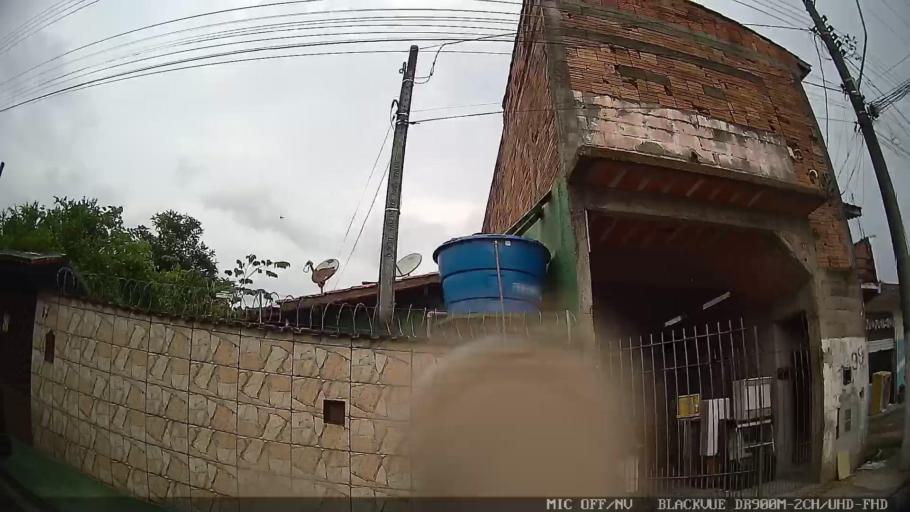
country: BR
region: Sao Paulo
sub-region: Caraguatatuba
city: Caraguatatuba
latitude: -23.6476
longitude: -45.4290
